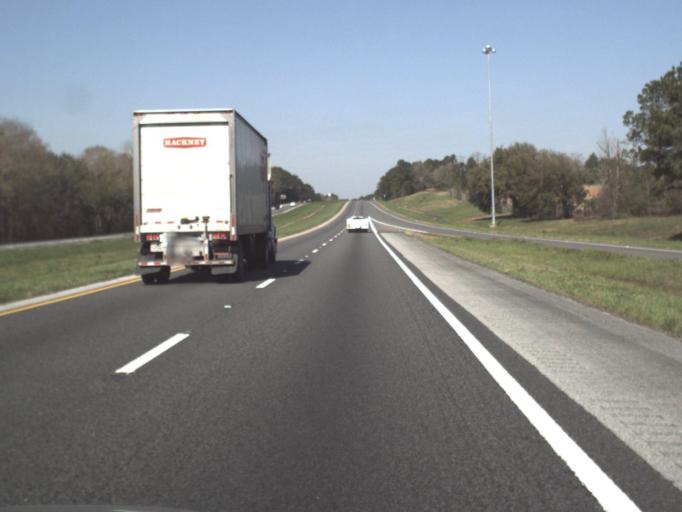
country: US
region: Florida
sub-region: Jackson County
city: Sneads
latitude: 30.6594
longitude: -85.0420
